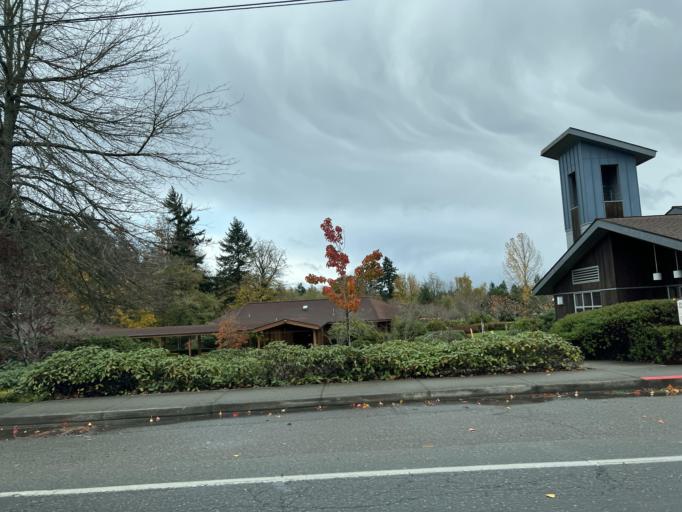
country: US
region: Washington
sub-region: Kitsap County
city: Bainbridge Island
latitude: 47.6368
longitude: -122.5210
